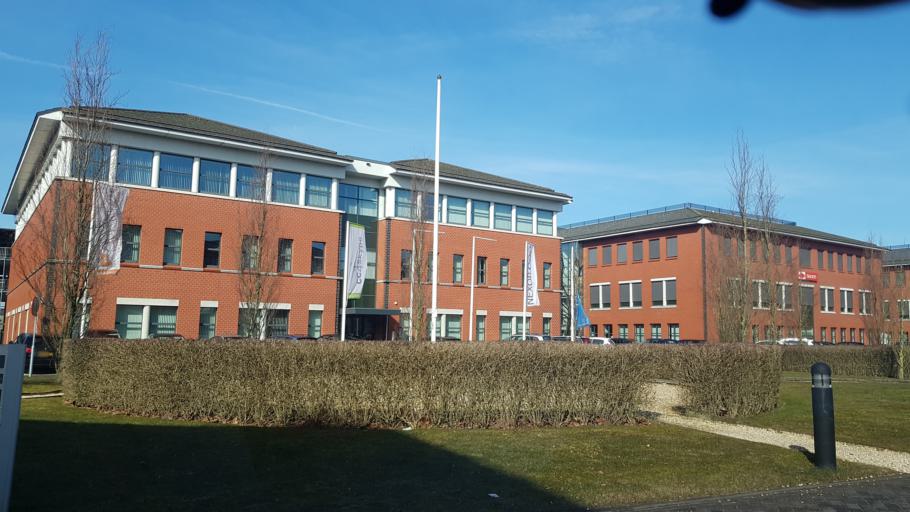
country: NL
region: Utrecht
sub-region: Gemeente Vianen
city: Vianen
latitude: 51.9837
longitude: 5.1056
